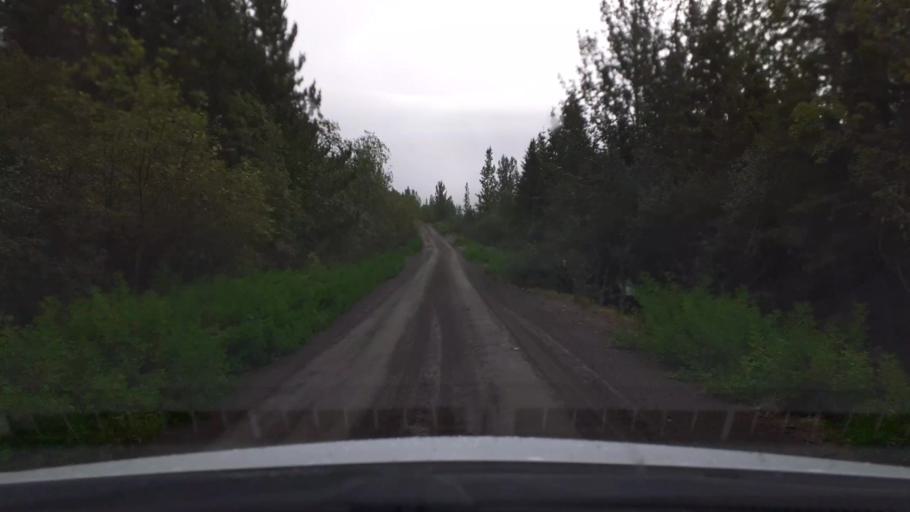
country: IS
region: Capital Region
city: Mosfellsbaer
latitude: 64.4927
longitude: -21.3438
